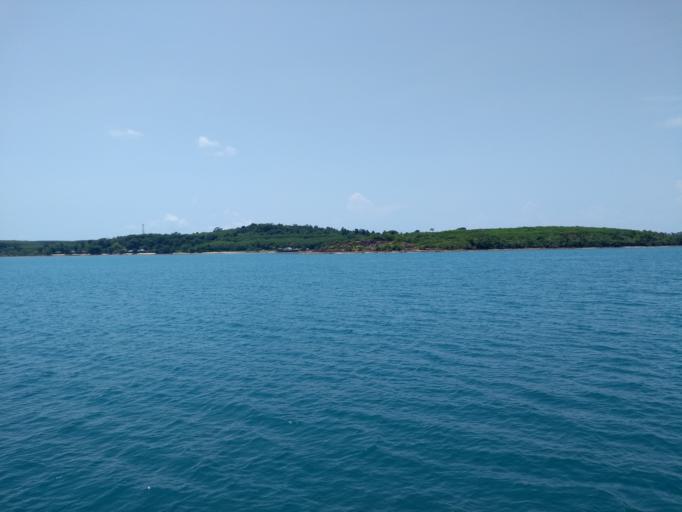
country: TH
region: Trat
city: Ko Kut
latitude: 11.8071
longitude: 102.5056
